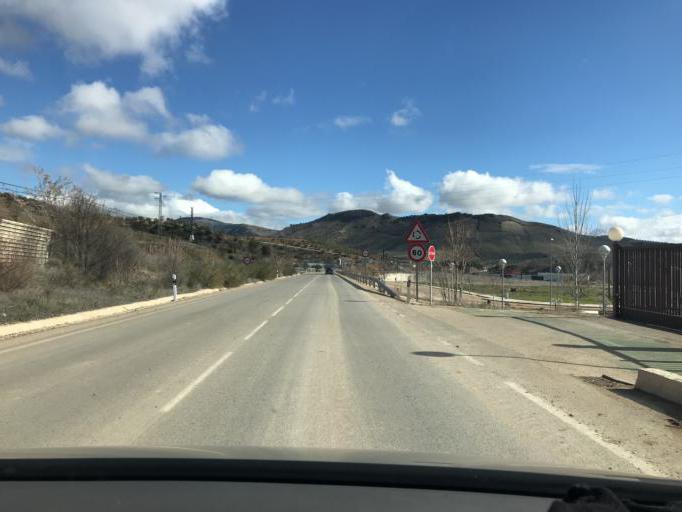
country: ES
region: Andalusia
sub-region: Provincia de Jaen
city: Huelma
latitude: 37.6488
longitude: -3.4354
